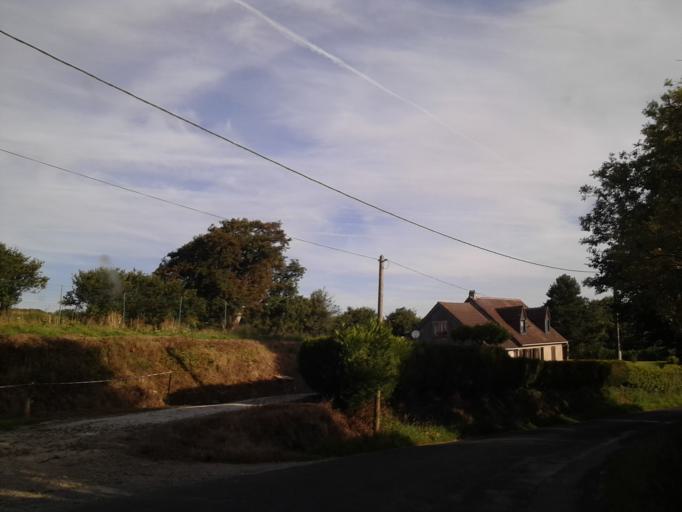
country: FR
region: Lower Normandy
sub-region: Departement de la Manche
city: Fermanville
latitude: 49.6674
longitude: -1.4556
